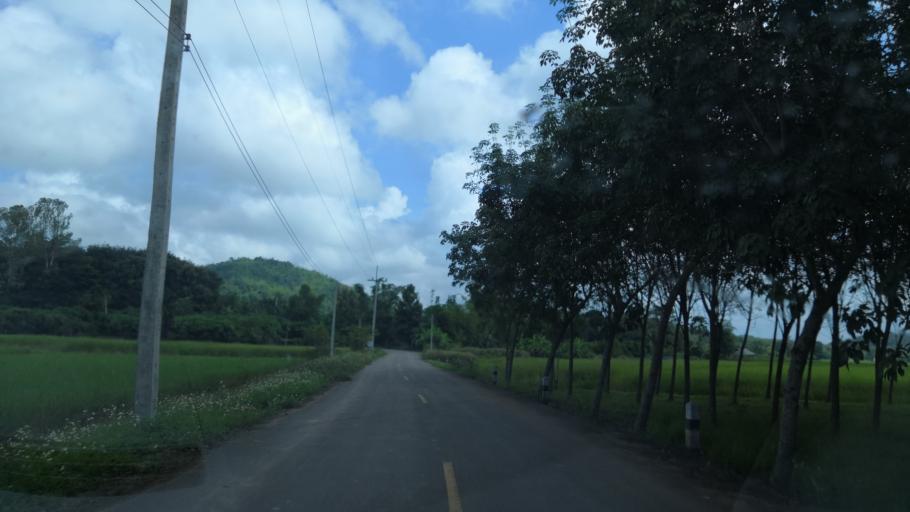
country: TH
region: Chiang Rai
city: Wiang Chiang Rung
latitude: 20.0215
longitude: 100.0441
